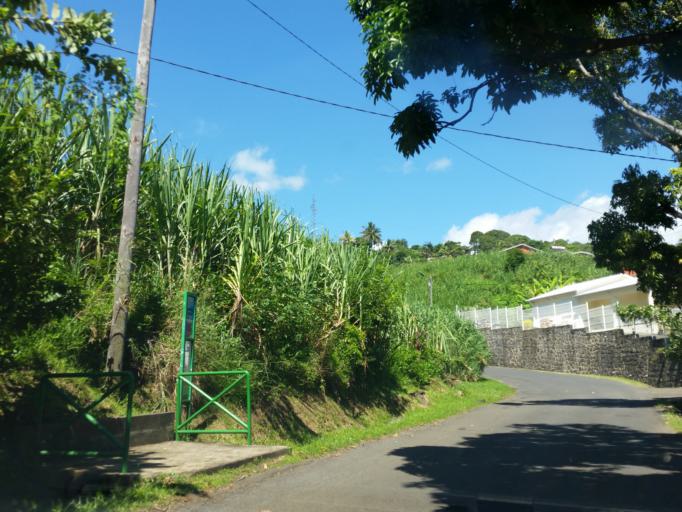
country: RE
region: Reunion
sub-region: Reunion
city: Sainte-Marie
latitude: -20.9354
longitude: 55.5279
